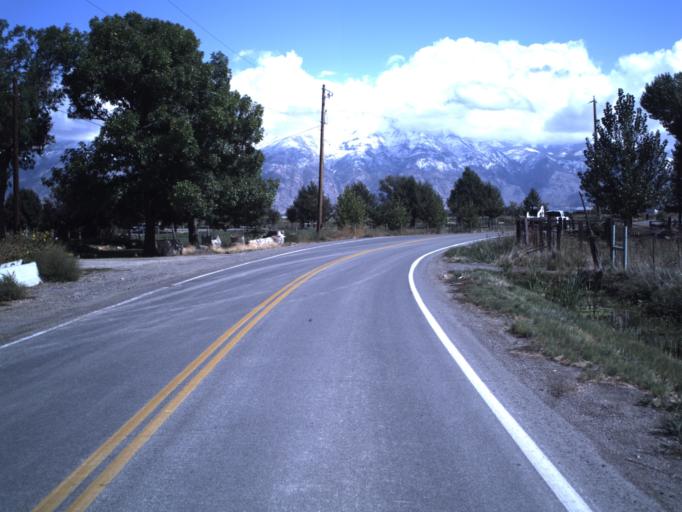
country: US
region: Utah
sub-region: Utah County
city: Benjamin
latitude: 40.1581
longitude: -111.7120
